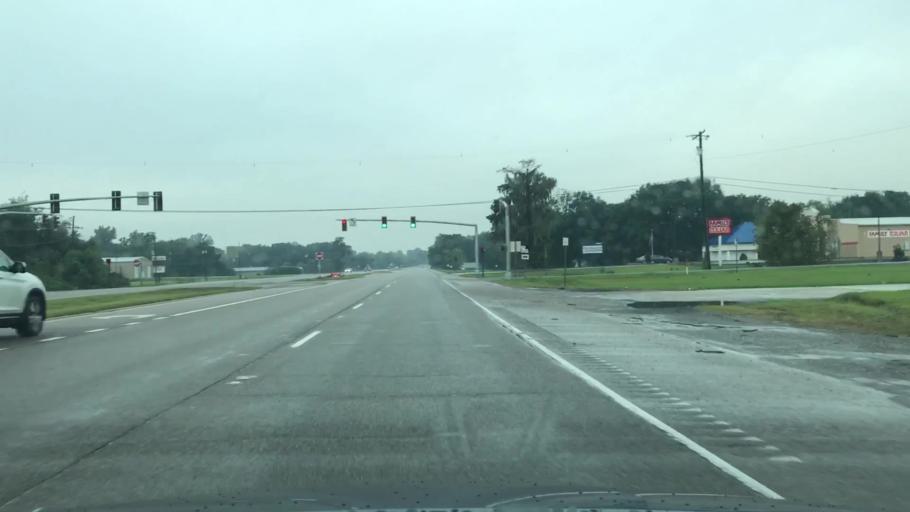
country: US
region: Louisiana
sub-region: Saint Charles Parish
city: Des Allemands
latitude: 29.8250
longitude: -90.4649
